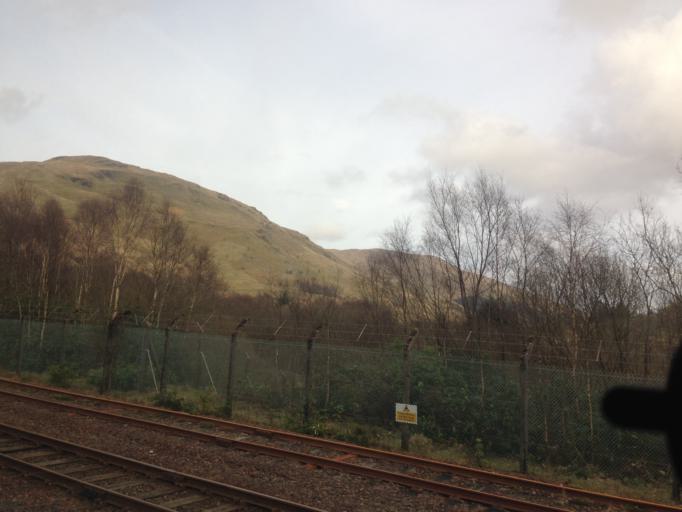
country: GB
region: Scotland
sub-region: Argyll and Bute
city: Garelochhead
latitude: 56.1562
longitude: -4.7800
